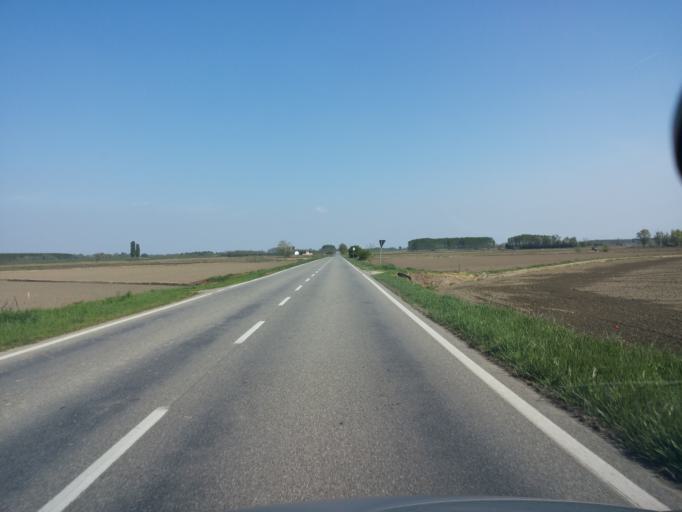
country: IT
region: Piedmont
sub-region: Provincia di Vercelli
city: Caresana
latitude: 45.2120
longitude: 8.5174
